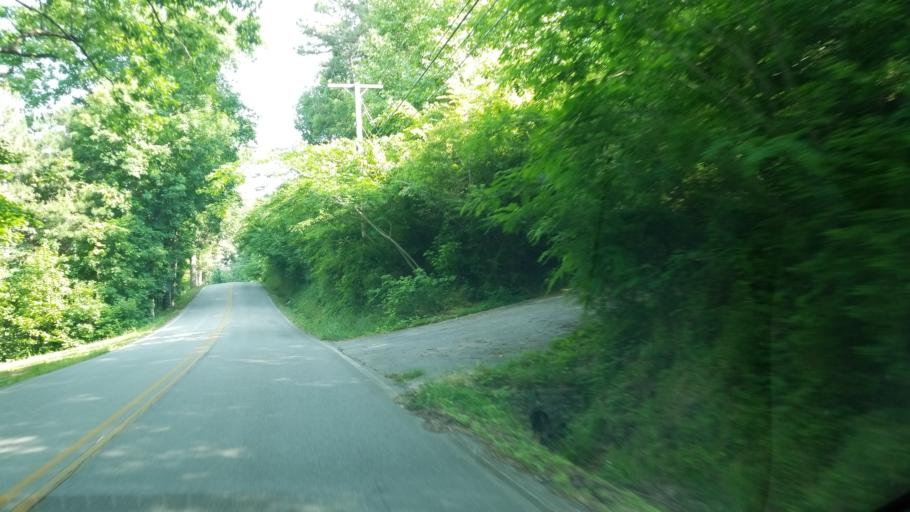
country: US
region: Tennessee
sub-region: Hamilton County
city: Collegedale
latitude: 35.0840
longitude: -85.0100
